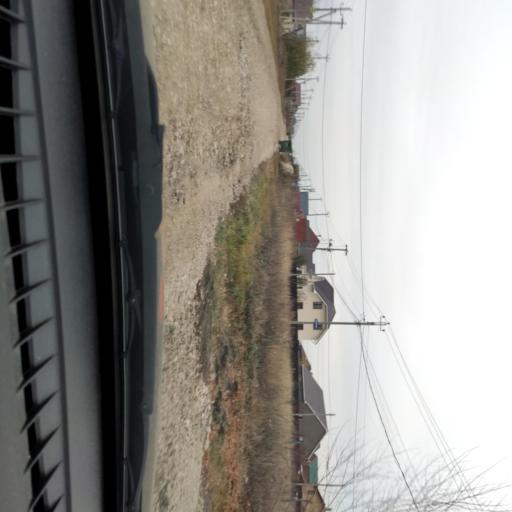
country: RU
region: Samara
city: Podstepki
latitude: 53.5250
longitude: 49.1543
